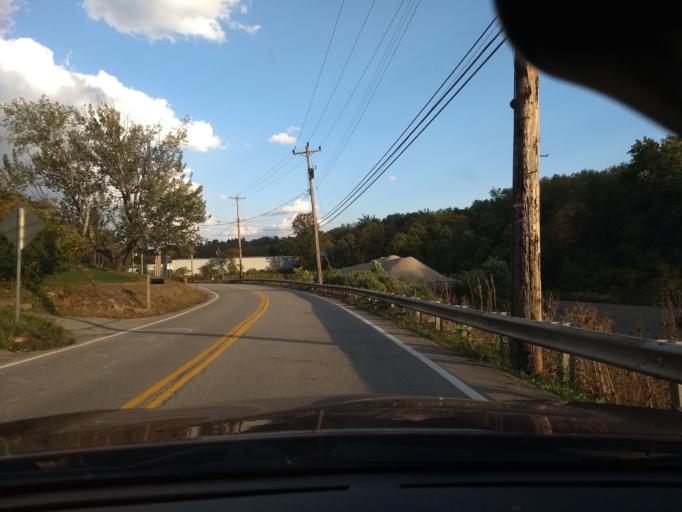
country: US
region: Pennsylvania
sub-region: Allegheny County
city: Dravosburg
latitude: 40.3670
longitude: -79.8873
